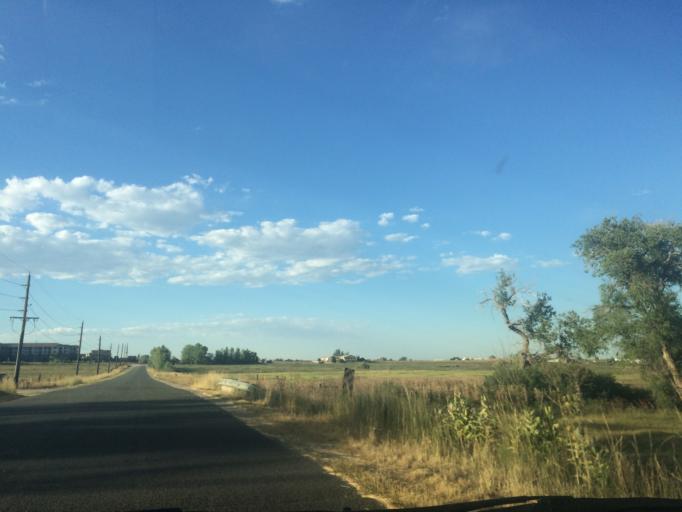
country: US
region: Colorado
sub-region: Broomfield County
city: Broomfield
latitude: 39.9389
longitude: -105.1187
